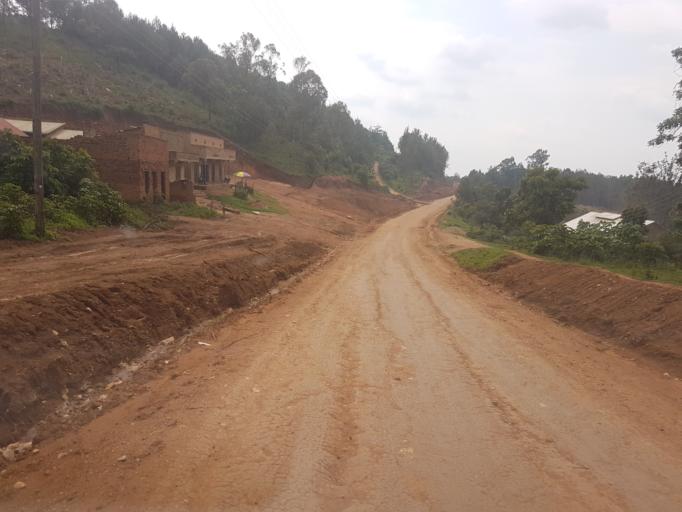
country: UG
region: Western Region
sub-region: Kanungu District
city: Ntungamo
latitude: -0.8269
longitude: 29.7095
